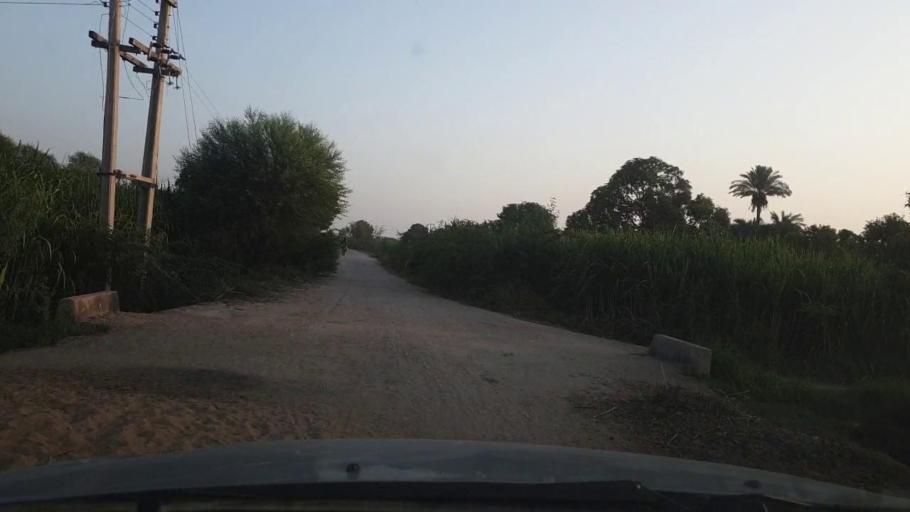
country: PK
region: Sindh
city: Tando Ghulam Ali
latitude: 25.1486
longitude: 68.9747
